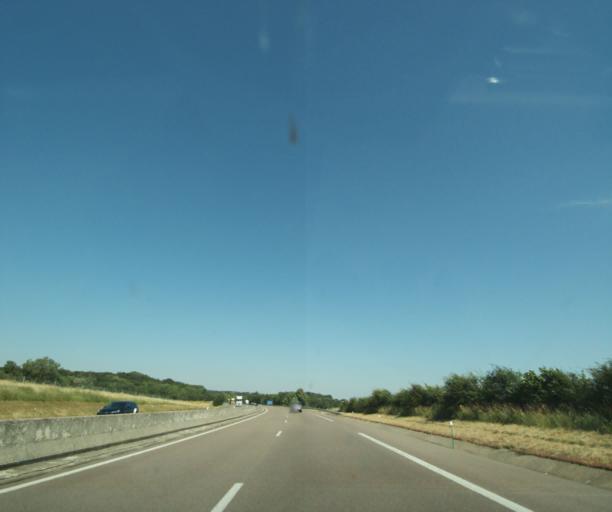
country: FR
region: Lorraine
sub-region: Departement des Vosges
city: Chatenois
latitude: 48.4047
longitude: 5.8775
